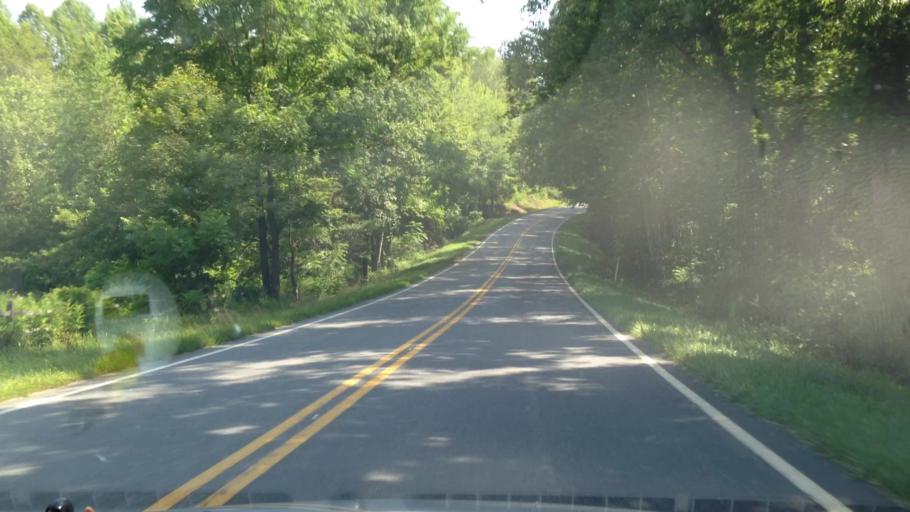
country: US
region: North Carolina
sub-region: Surry County
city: Flat Rock
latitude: 36.5671
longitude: -80.4617
